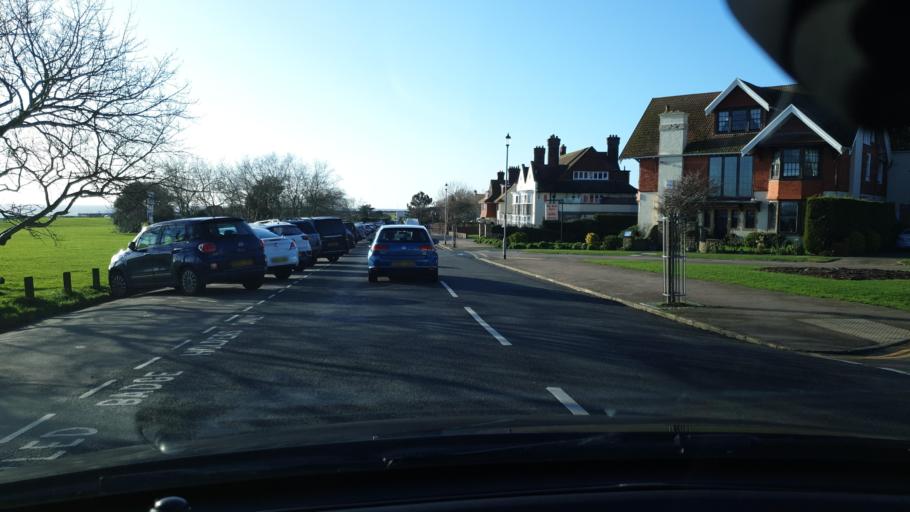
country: GB
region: England
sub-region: Essex
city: Frinton-on-Sea
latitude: 51.8263
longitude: 1.2430
